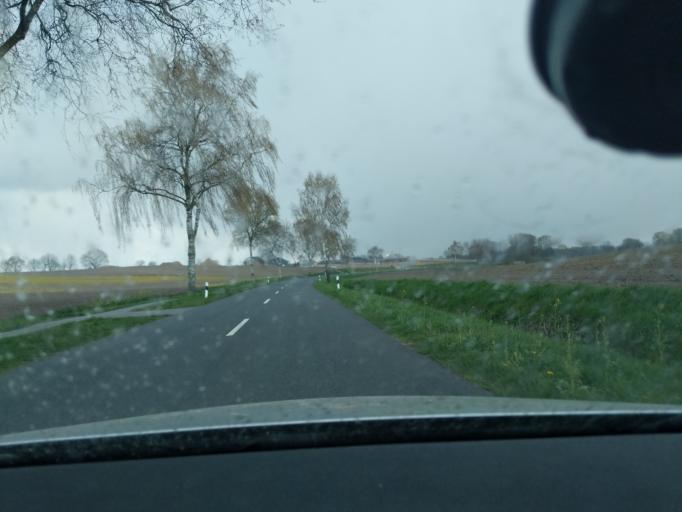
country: DE
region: Lower Saxony
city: Horneburg
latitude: 53.5101
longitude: 9.5535
